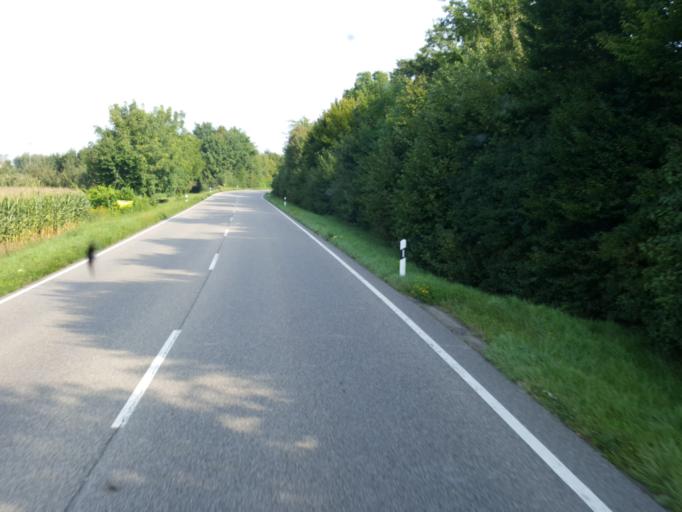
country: DE
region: Baden-Wuerttemberg
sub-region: Karlsruhe Region
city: Sinzheim
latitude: 48.7506
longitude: 8.1671
